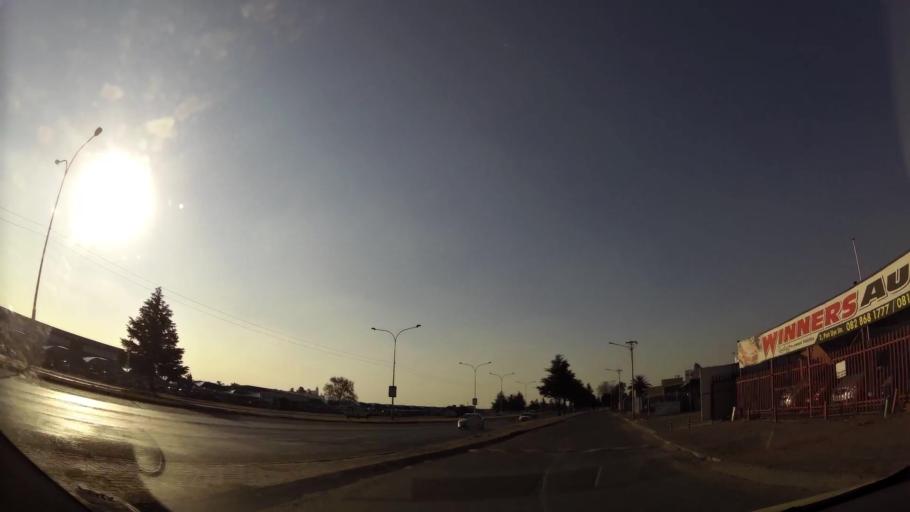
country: ZA
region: Gauteng
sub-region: West Rand District Municipality
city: Randfontein
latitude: -26.1994
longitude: 27.6983
